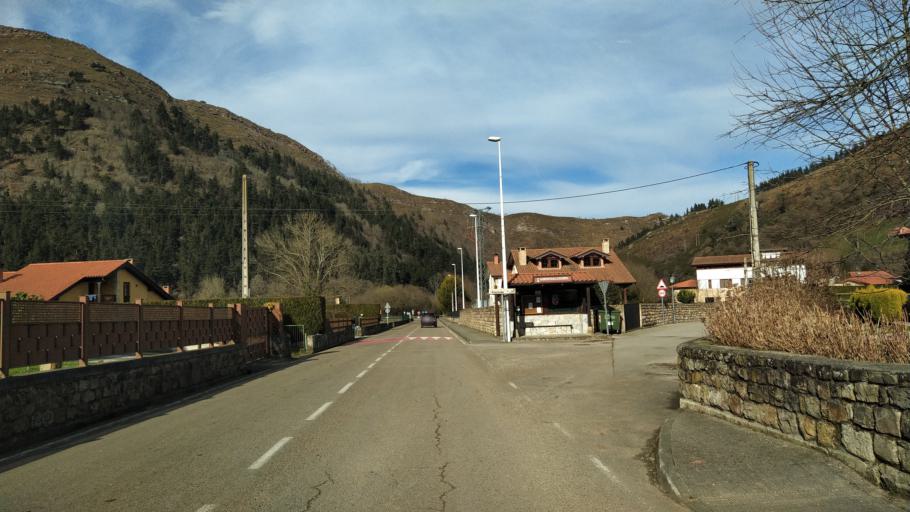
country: ES
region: Cantabria
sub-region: Provincia de Cantabria
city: Ruente
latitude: 43.2673
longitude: -4.2491
